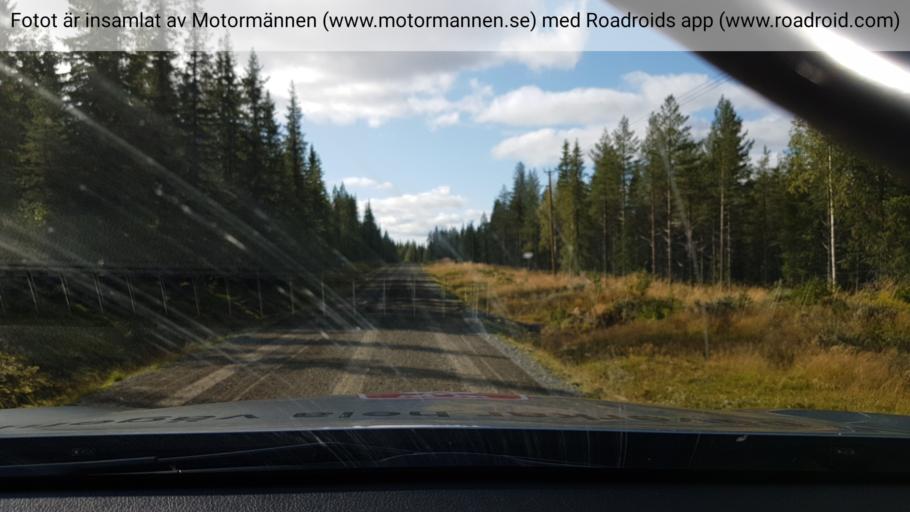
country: SE
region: Vaesterbotten
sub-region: Mala Kommun
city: Mala
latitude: 65.4876
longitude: 18.2371
